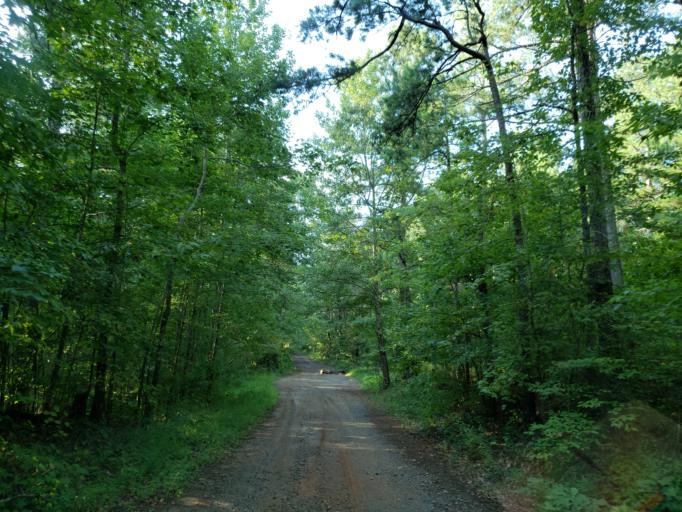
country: US
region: Georgia
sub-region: Cobb County
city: Acworth
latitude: 34.1790
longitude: -84.6452
